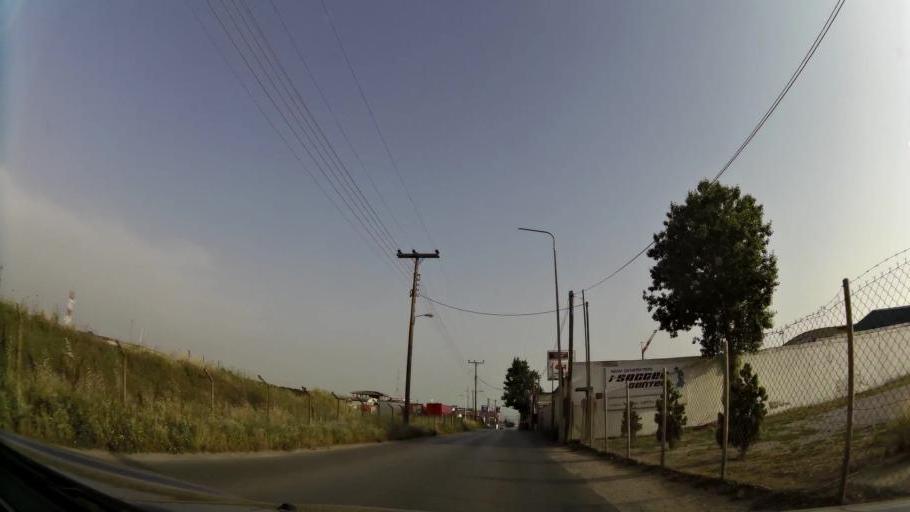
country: GR
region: Central Macedonia
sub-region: Nomos Thessalonikis
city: Evosmos
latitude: 40.6891
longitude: 22.9060
